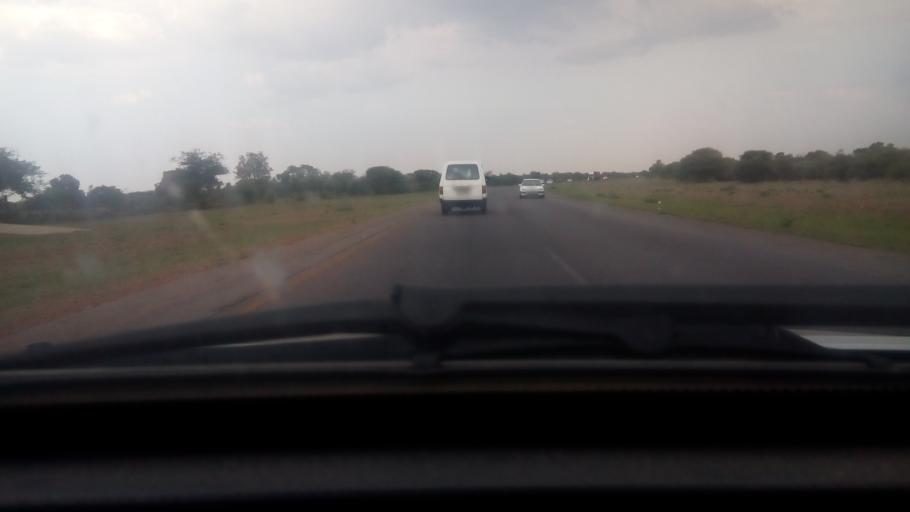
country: BW
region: Kweneng
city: Molepolole
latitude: -24.4486
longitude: 25.6403
